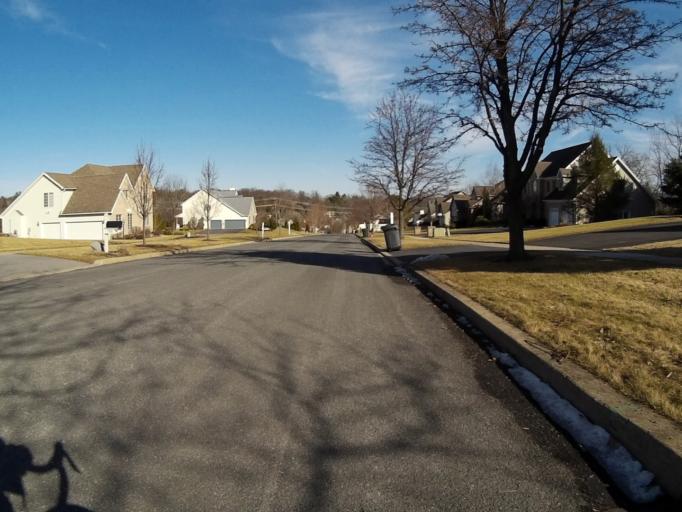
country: US
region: Pennsylvania
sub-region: Centre County
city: State College
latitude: 40.7919
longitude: -77.8852
